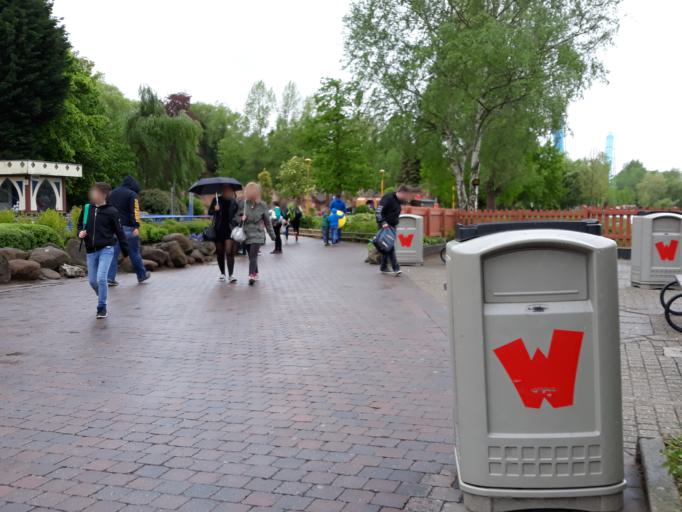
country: BE
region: Wallonia
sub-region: Province du Brabant Wallon
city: Wavre
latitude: 50.7001
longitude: 4.5940
